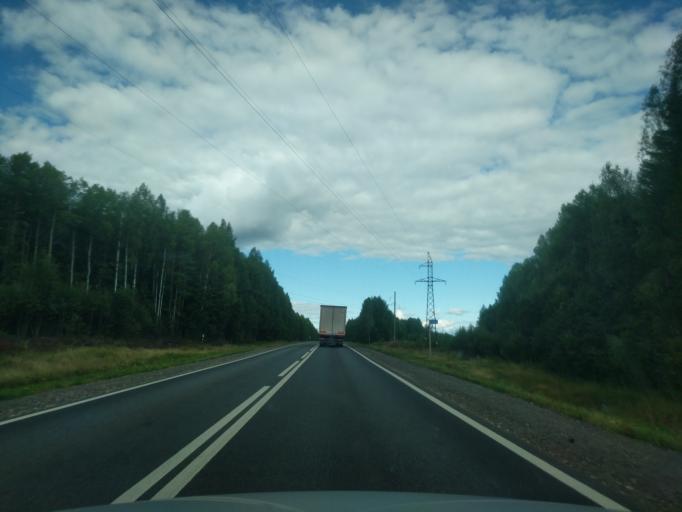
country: RU
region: Kostroma
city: Kadyy
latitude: 57.8458
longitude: 43.4616
